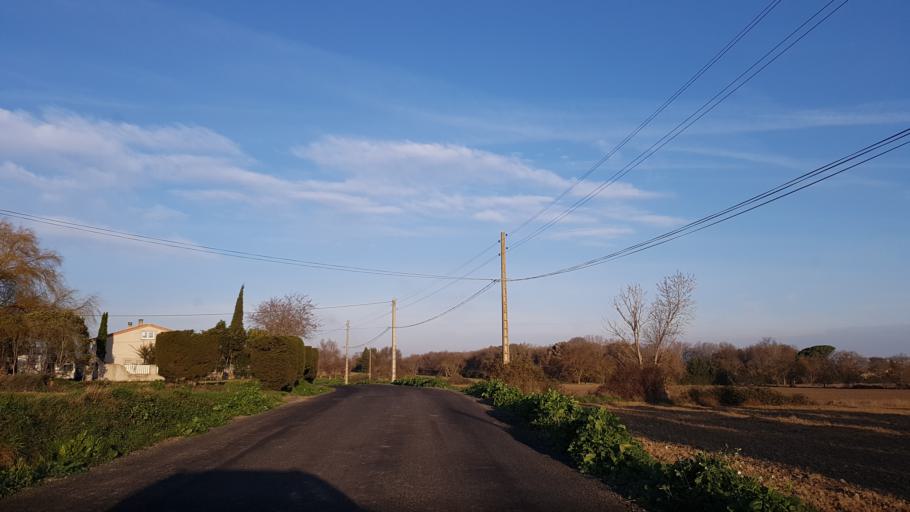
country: FR
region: Languedoc-Roussillon
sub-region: Departement de l'Aude
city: Villeneuve-la-Comptal
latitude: 43.2772
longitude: 1.9429
